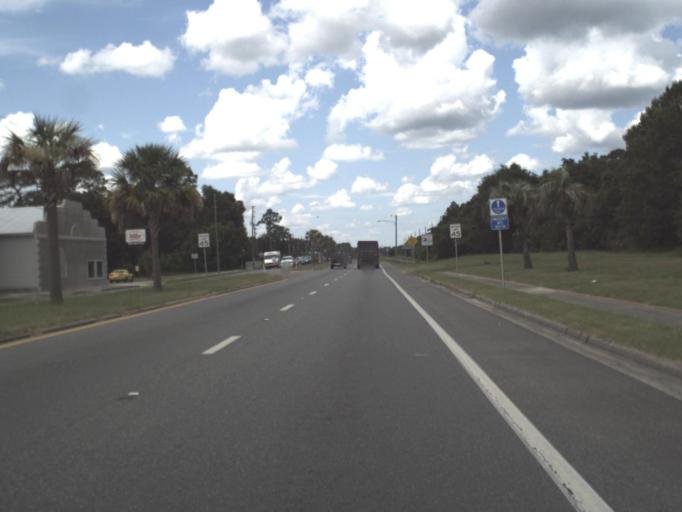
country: US
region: Florida
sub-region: Taylor County
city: Perry
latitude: 30.1188
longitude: -83.5900
